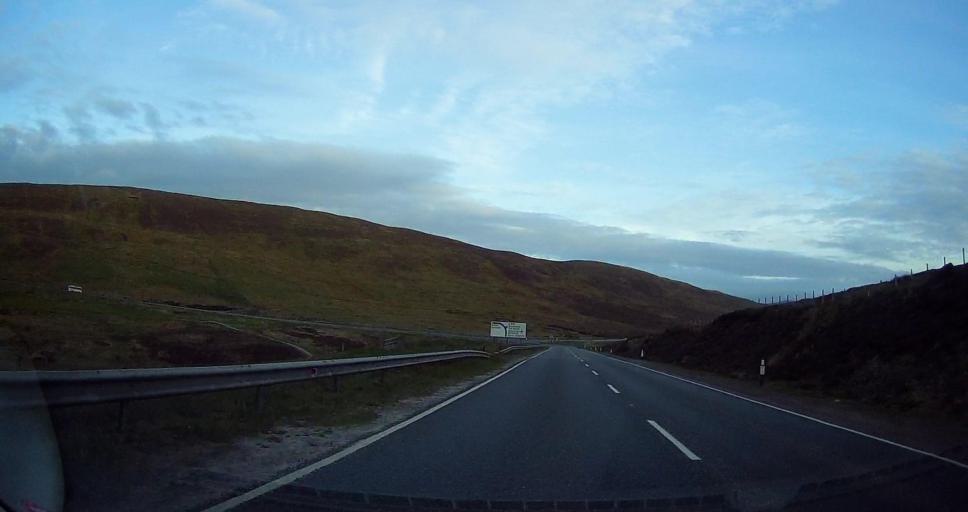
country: GB
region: Scotland
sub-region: Shetland Islands
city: Lerwick
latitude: 60.1631
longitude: -1.2273
